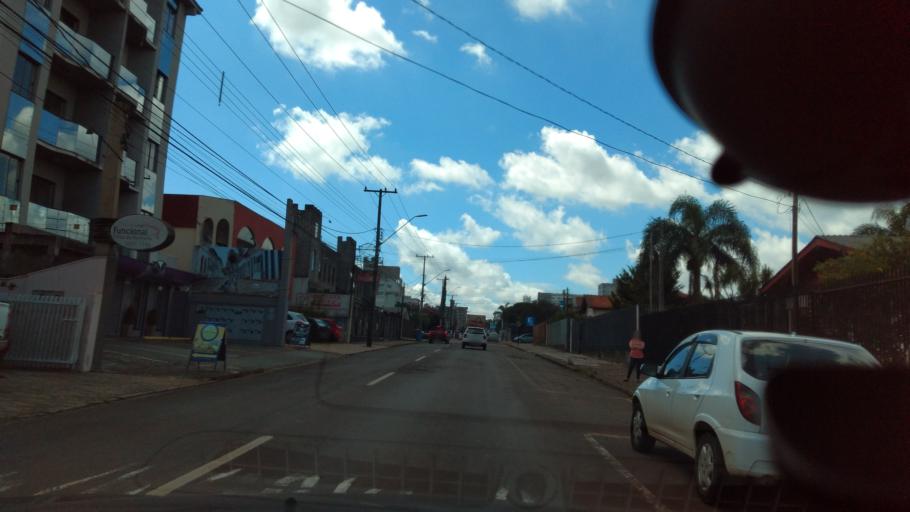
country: BR
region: Parana
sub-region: Guarapuava
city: Guarapuava
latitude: -25.3868
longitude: -51.4785
